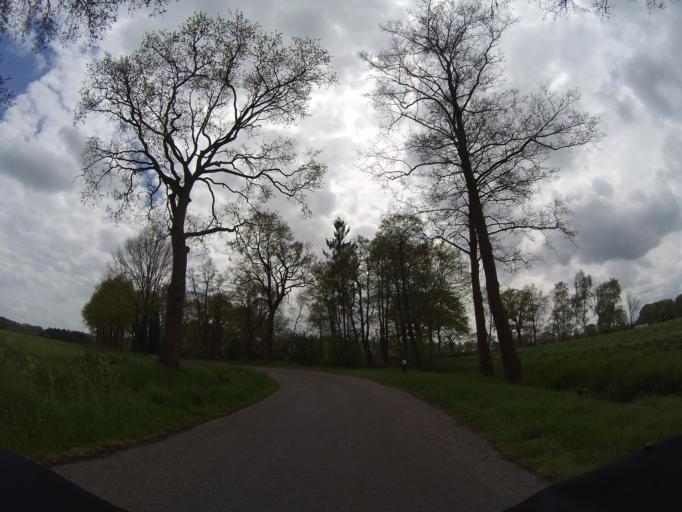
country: NL
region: Overijssel
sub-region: Gemeente Hardenberg
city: Hardenberg
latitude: 52.5421
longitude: 6.5823
